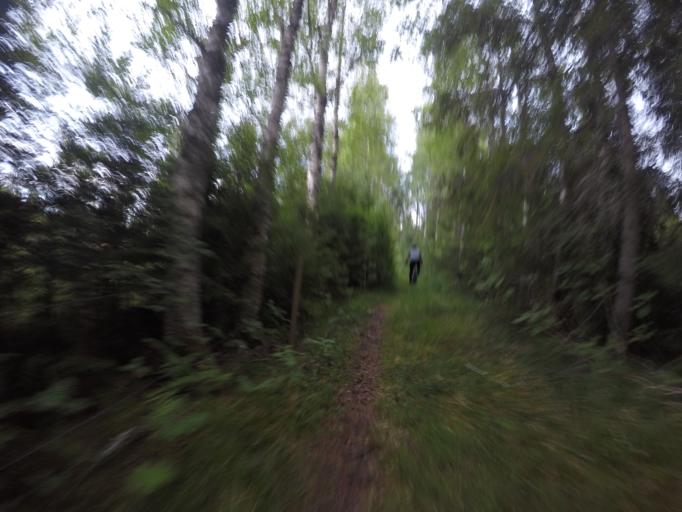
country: SE
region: OErebro
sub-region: Hallefors Kommun
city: Haellefors
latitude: 60.0406
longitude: 14.5059
